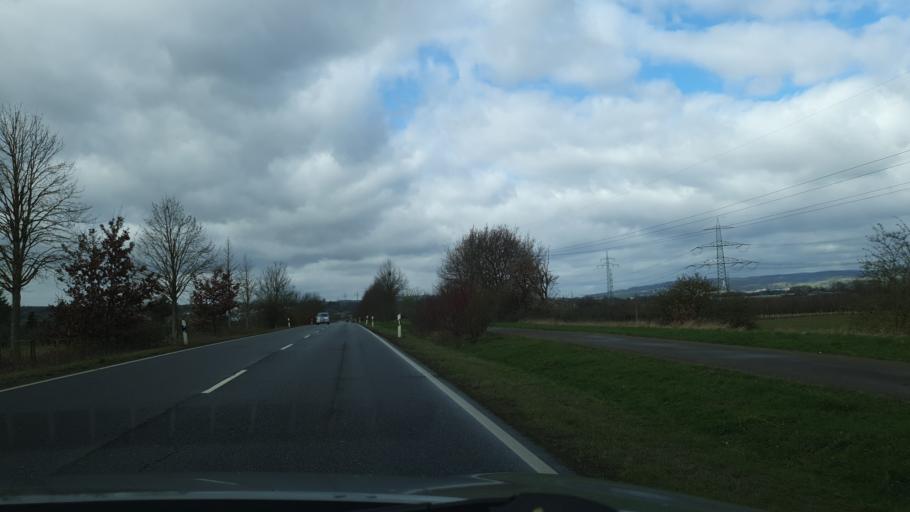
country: DE
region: Rheinland-Pfalz
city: Mulheim-Karlich
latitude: 50.3935
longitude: 7.4921
